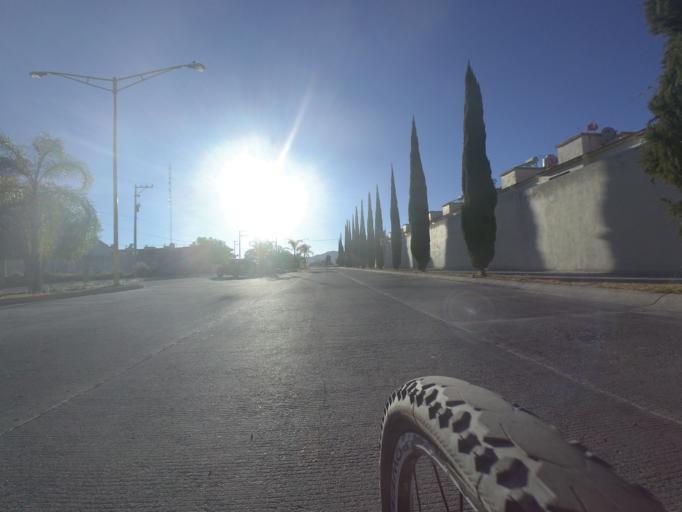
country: MX
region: Aguascalientes
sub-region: Aguascalientes
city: La Loma de los Negritos
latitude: 21.8543
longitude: -102.3448
